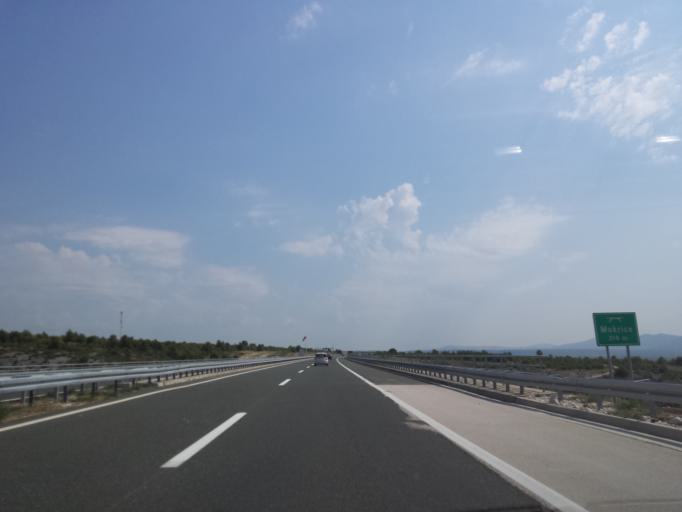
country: HR
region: Sibensko-Kniniska
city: Zaton
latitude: 43.8545
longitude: 15.8520
